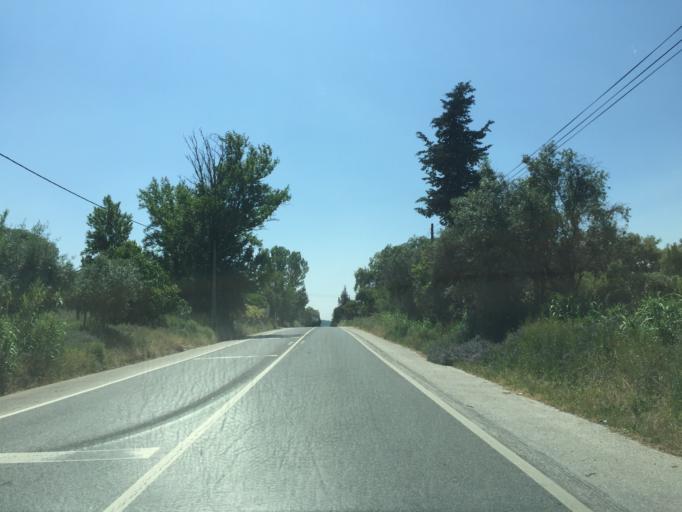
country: PT
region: Santarem
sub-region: Constancia
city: Constancia
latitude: 39.4699
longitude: -8.3313
